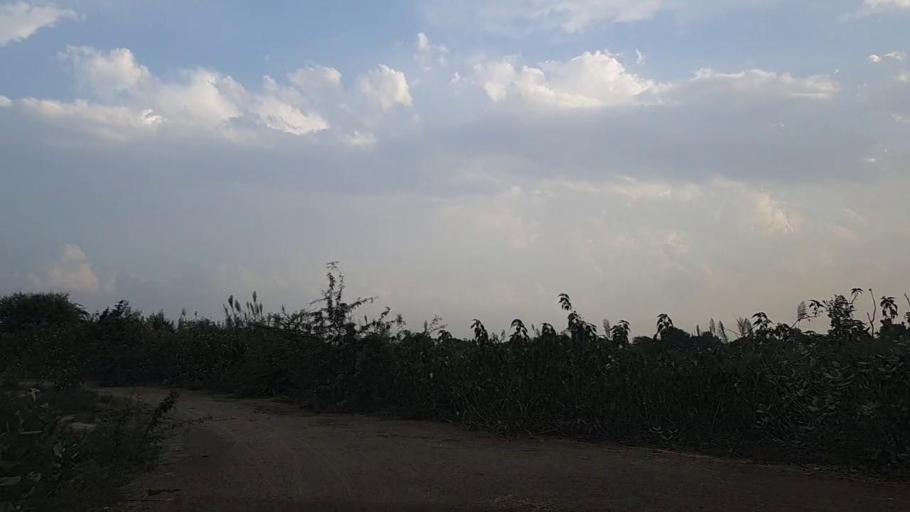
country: PK
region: Sindh
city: Daro Mehar
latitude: 24.7691
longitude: 68.1424
